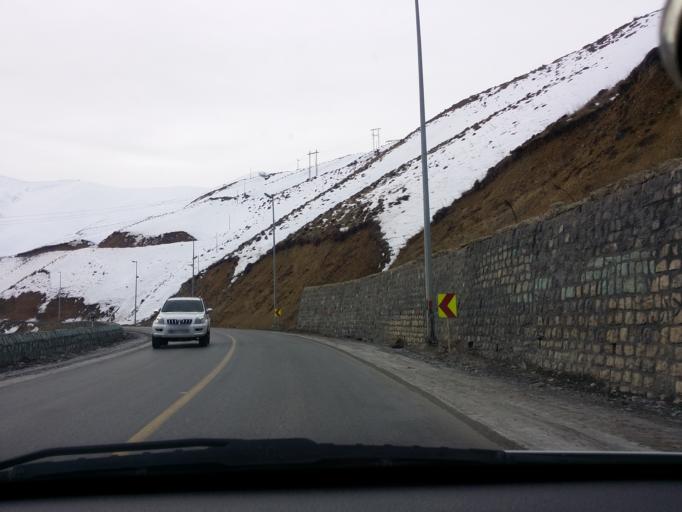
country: IR
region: Tehran
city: Tajrish
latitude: 36.1651
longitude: 51.3154
